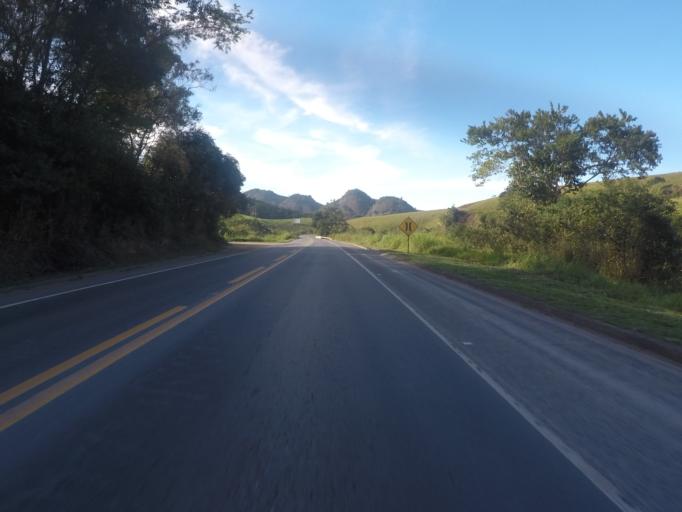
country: BR
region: Espirito Santo
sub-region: Fundao
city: Fundao
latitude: -19.8745
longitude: -40.4137
